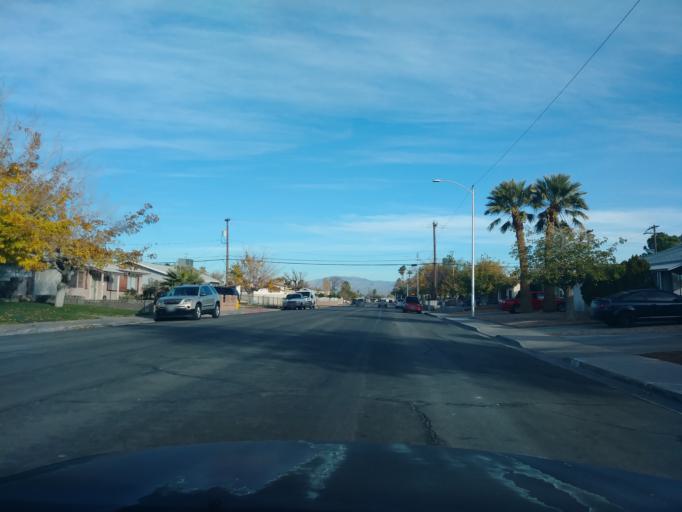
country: US
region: Nevada
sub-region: Clark County
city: Spring Valley
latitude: 36.1621
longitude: -115.2281
